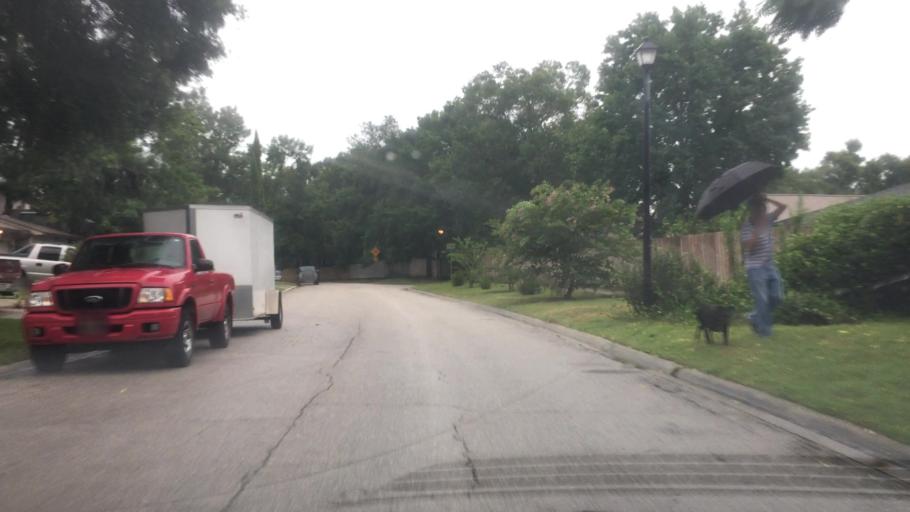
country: US
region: Florida
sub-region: Duval County
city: Jacksonville
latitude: 30.3399
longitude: -81.5337
